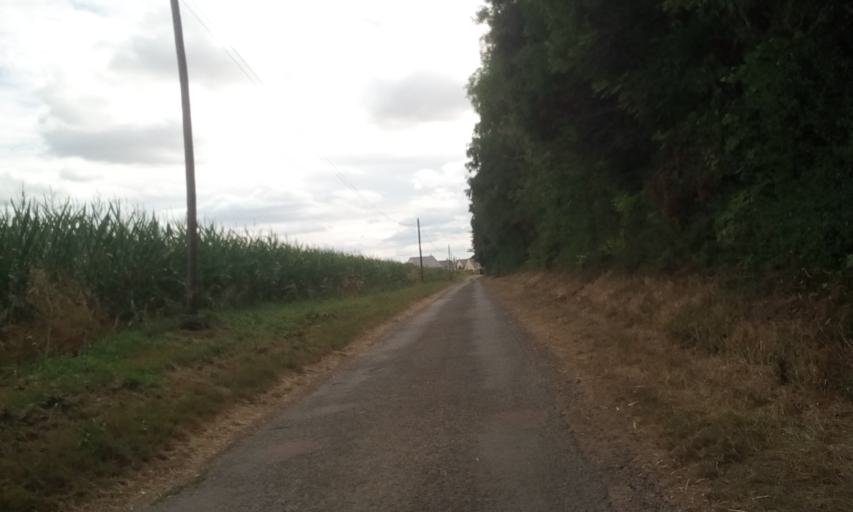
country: FR
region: Lower Normandy
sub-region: Departement du Calvados
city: Bellengreville
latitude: 49.1271
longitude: -0.1952
